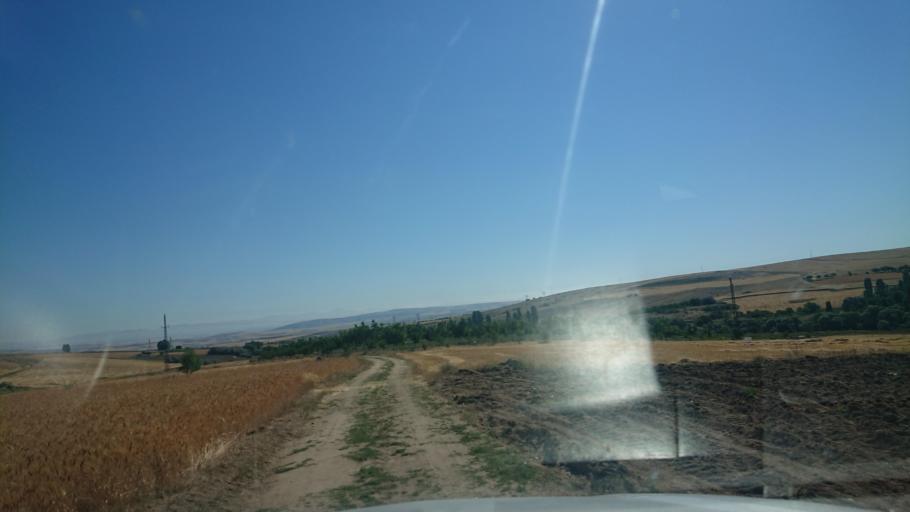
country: TR
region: Aksaray
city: Agacoren
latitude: 38.9000
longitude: 33.8988
